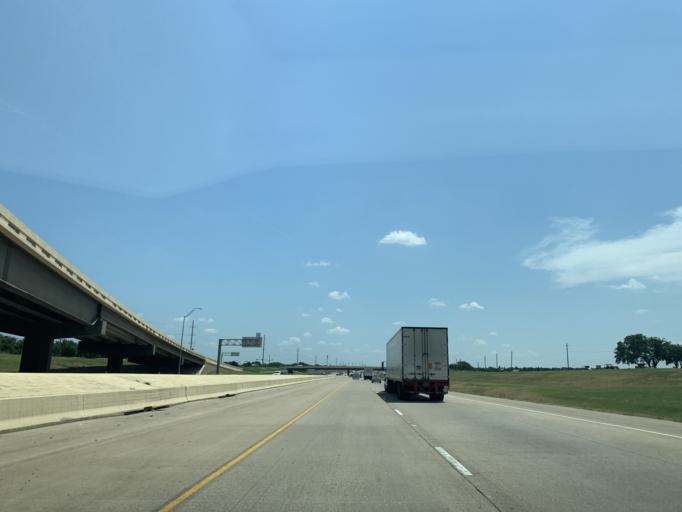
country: US
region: Texas
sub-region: Denton County
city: Roanoke
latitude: 32.9986
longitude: -97.2124
